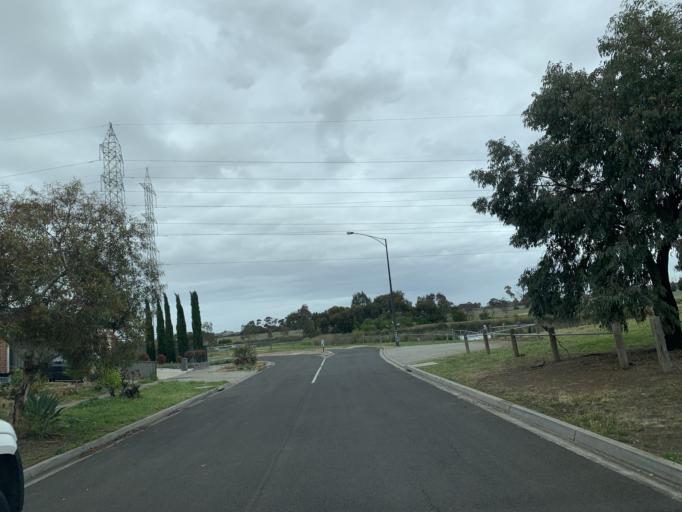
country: AU
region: Victoria
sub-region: Brimbank
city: St Albans
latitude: -37.7476
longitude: 144.7932
